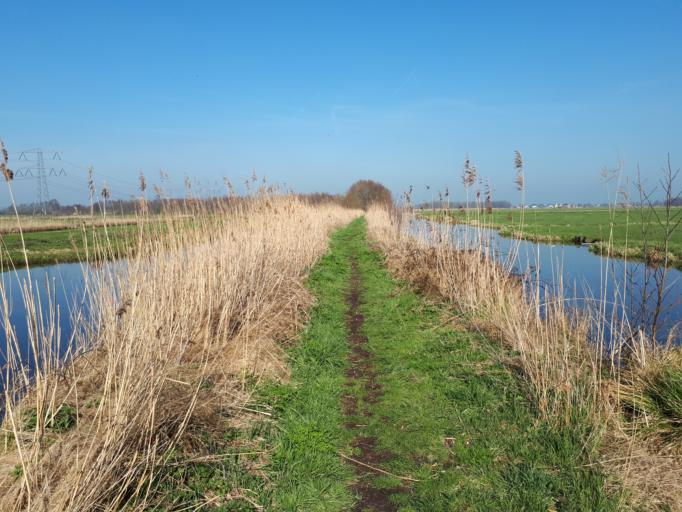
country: NL
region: South Holland
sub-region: Molenwaard
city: Nieuw-Lekkerland
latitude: 51.9420
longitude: 4.6770
